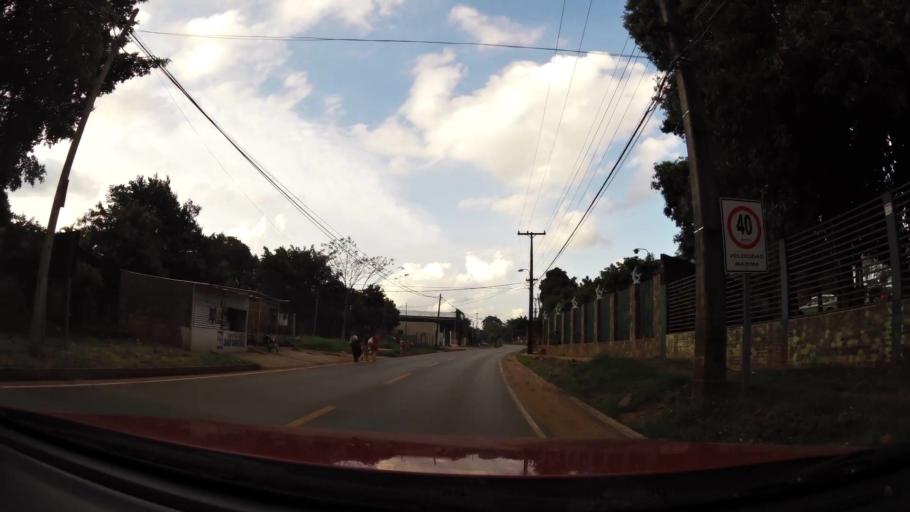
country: PY
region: Central
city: Nemby
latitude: -25.3712
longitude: -57.5433
